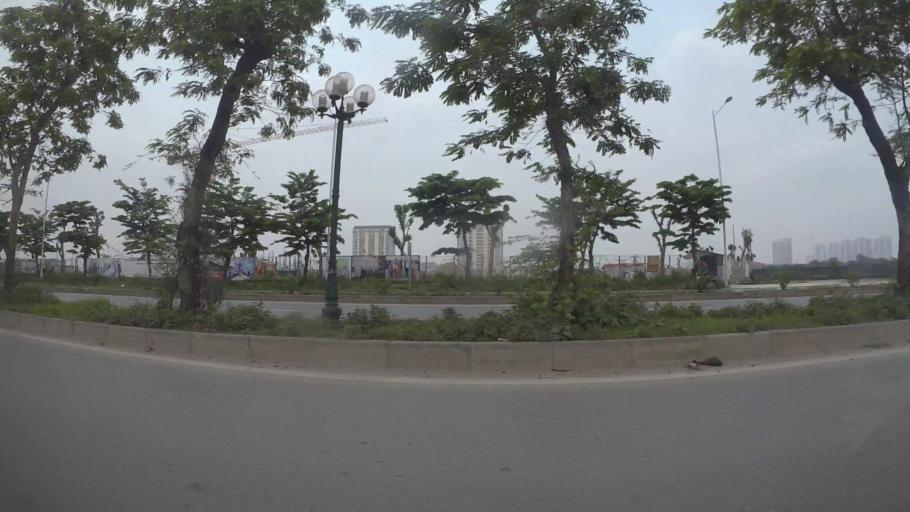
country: VN
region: Ha Noi
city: Cau Dien
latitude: 21.0367
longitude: 105.7491
